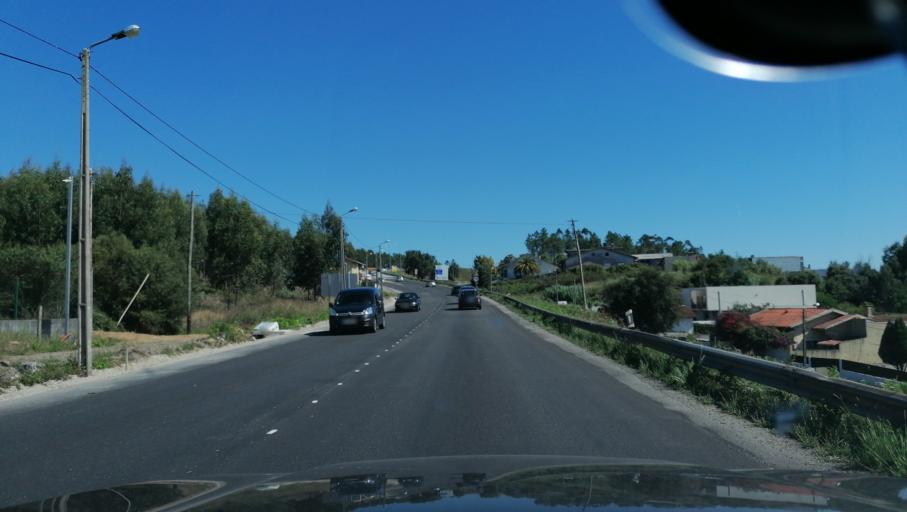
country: PT
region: Aveiro
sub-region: Santa Maria da Feira
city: Arrifana
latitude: 40.9268
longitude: -8.5085
